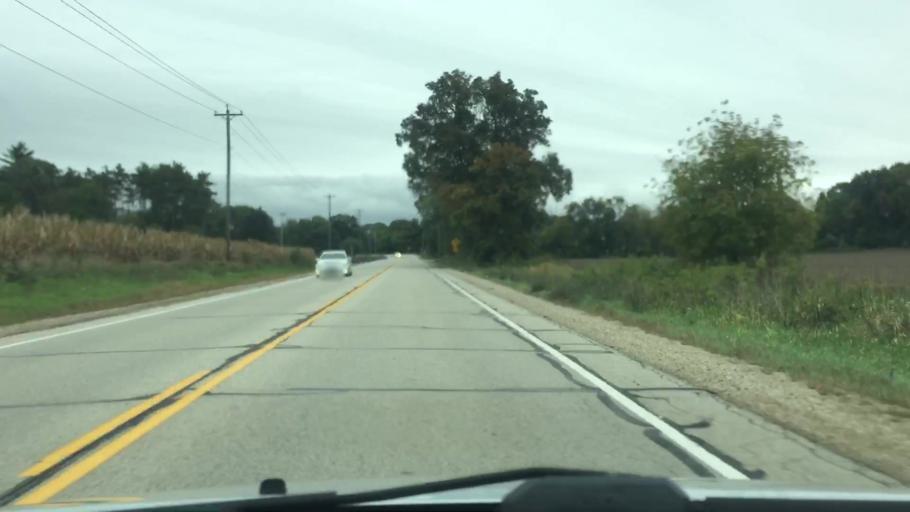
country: US
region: Wisconsin
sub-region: Jefferson County
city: Palmyra
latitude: 42.7921
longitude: -88.5631
